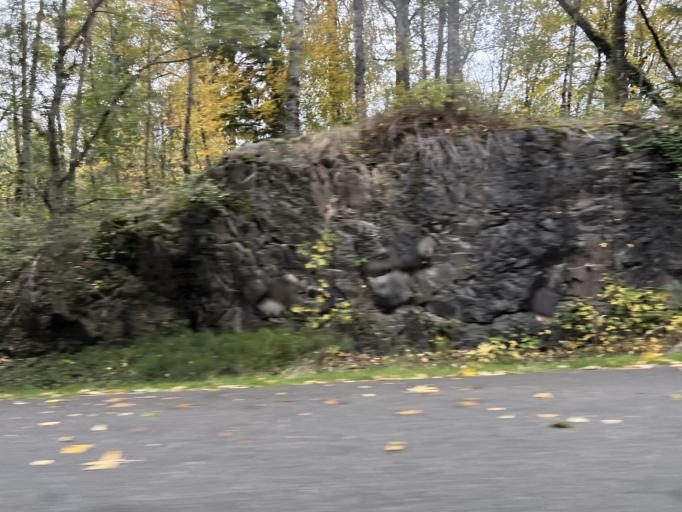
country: US
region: Washington
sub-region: King County
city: Snoqualmie
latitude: 47.5110
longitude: -121.8486
